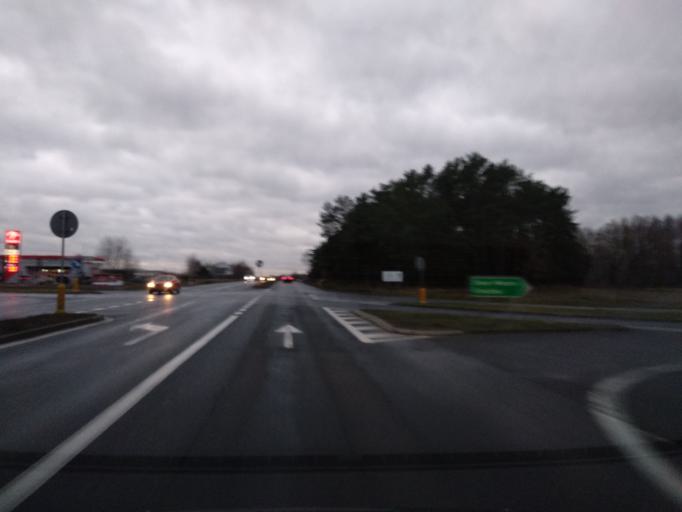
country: PL
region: Greater Poland Voivodeship
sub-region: Powiat koninski
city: Stare Miasto
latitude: 52.1707
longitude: 18.2138
